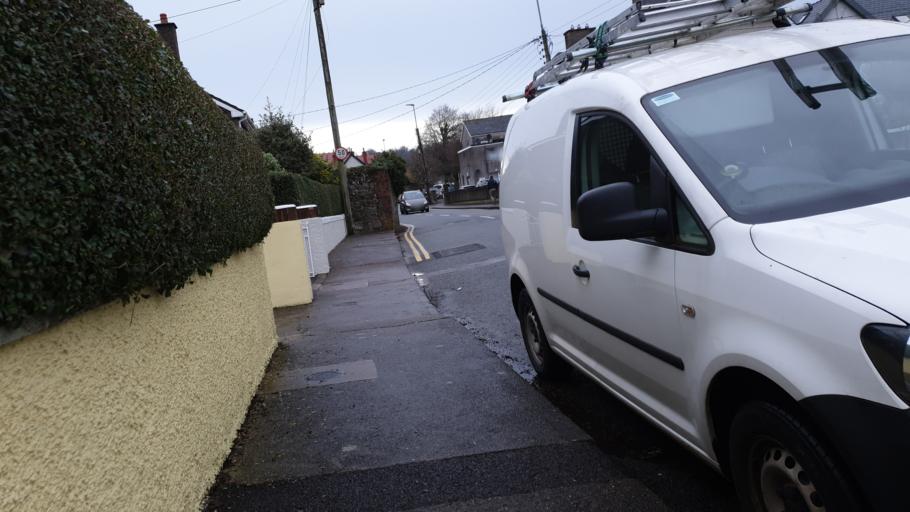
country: IE
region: Munster
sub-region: County Cork
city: Cork
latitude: 51.8953
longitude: -8.4311
